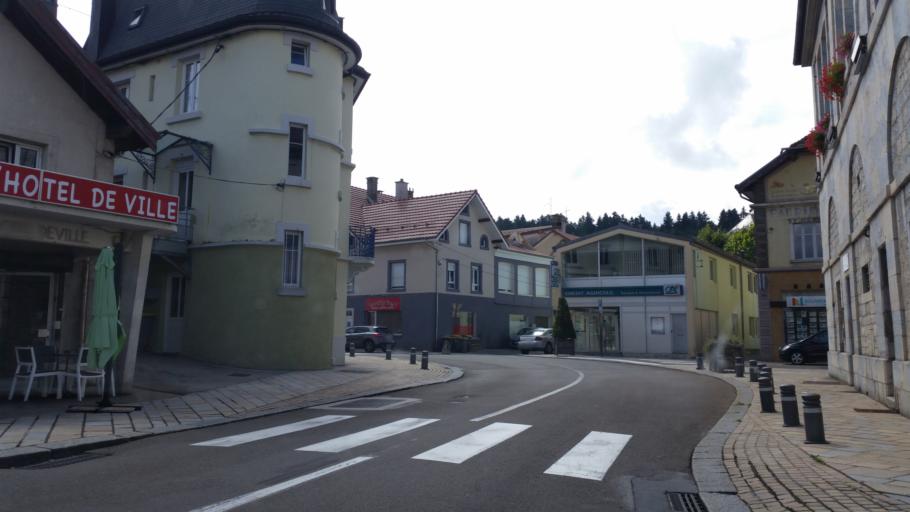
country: FR
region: Franche-Comte
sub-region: Departement du Doubs
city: Maiche
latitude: 47.2525
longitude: 6.8016
